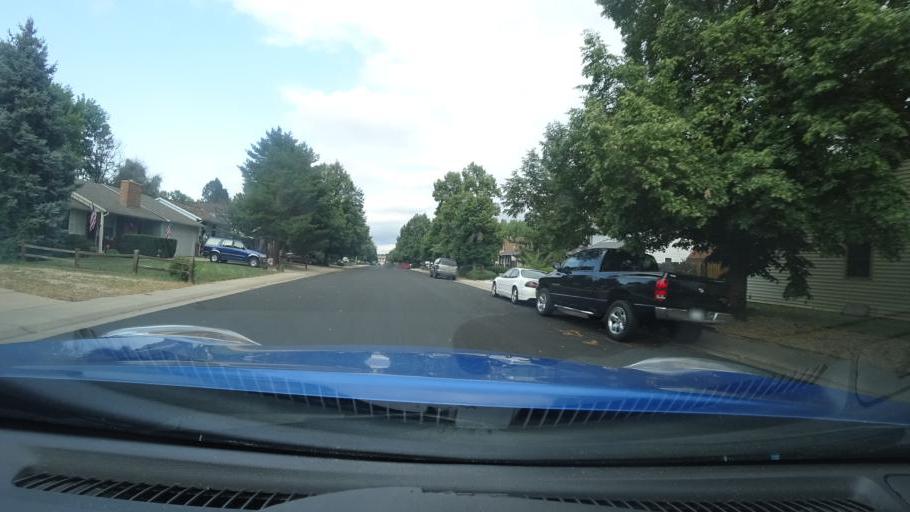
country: US
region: Colorado
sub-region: Adams County
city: Aurora
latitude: 39.6917
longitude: -104.8149
